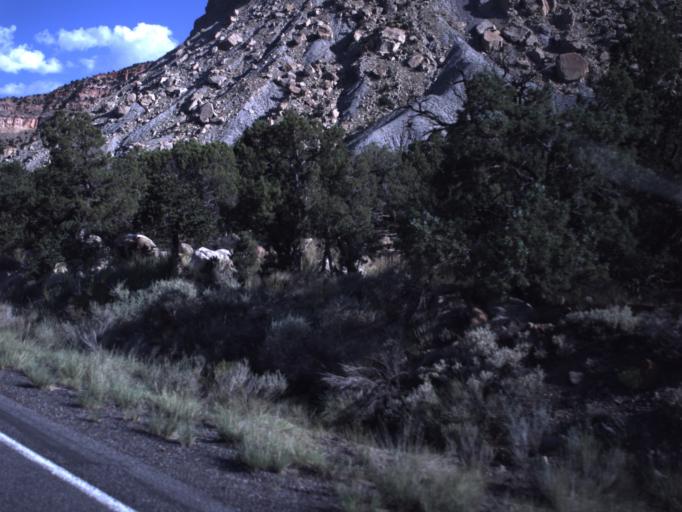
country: US
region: Utah
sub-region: Emery County
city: Huntington
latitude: 39.3878
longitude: -111.0841
